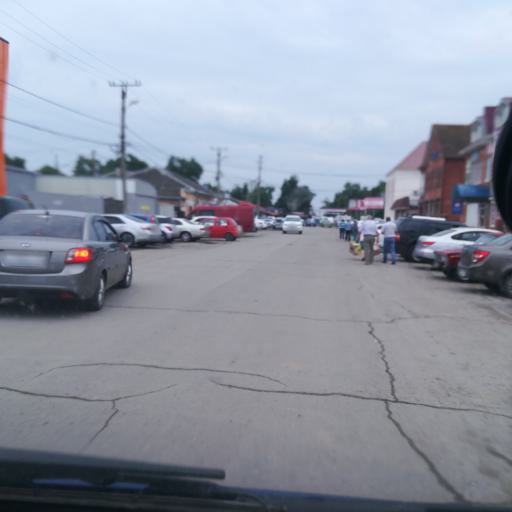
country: RU
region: Krasnodarskiy
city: Slavyansk-na-Kubani
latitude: 45.2633
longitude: 38.1299
